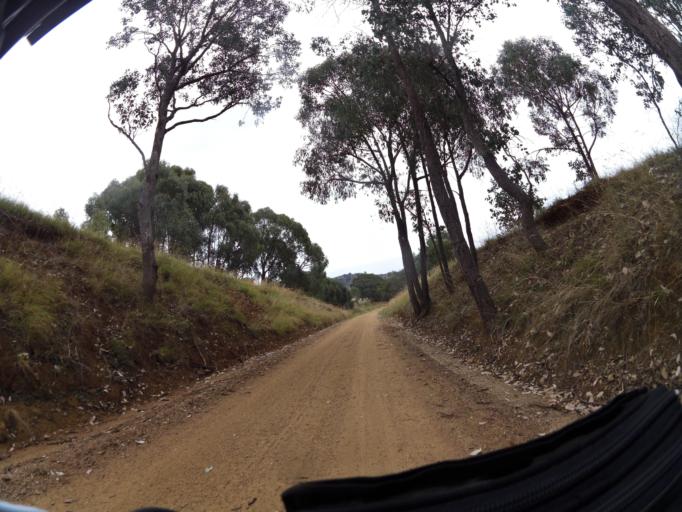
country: AU
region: New South Wales
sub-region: Albury Municipality
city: East Albury
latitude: -36.2004
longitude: 147.0446
